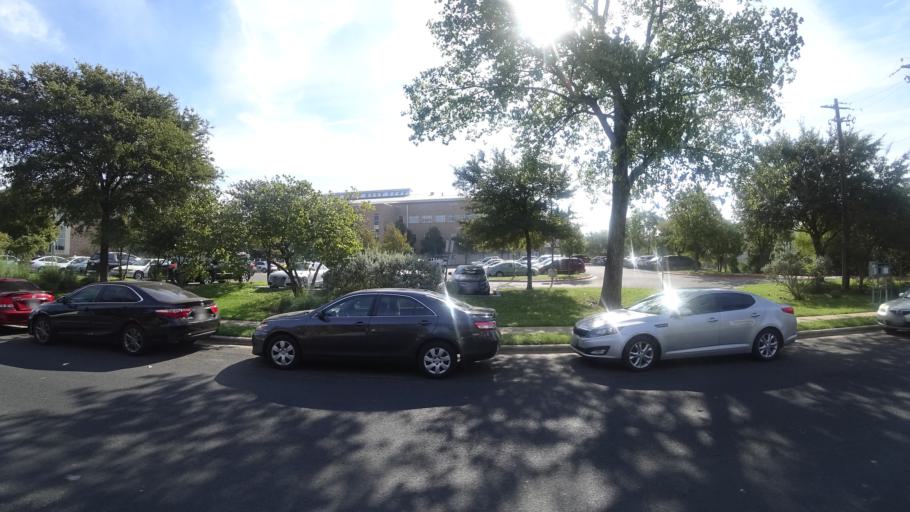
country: US
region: Texas
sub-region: Travis County
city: Austin
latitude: 30.2667
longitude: -97.7083
